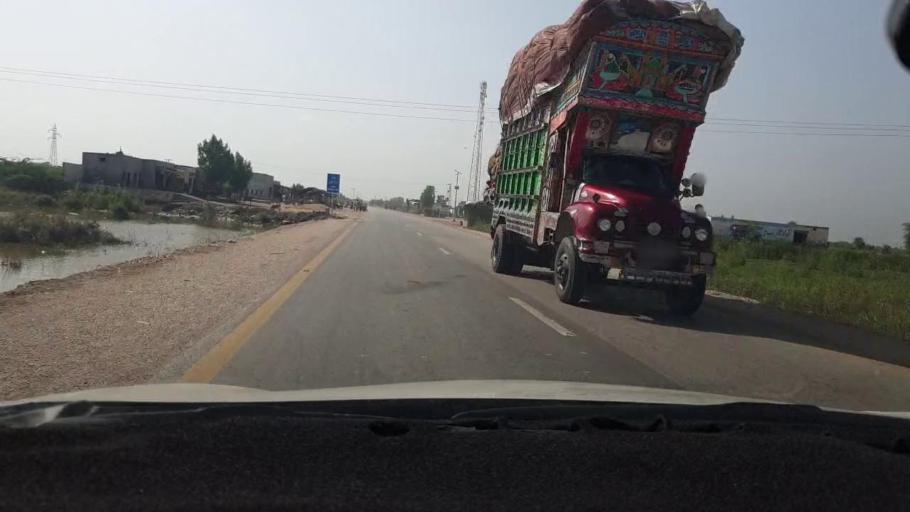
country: PK
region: Sindh
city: Tando Mittha Khan
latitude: 25.8283
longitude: 69.0643
